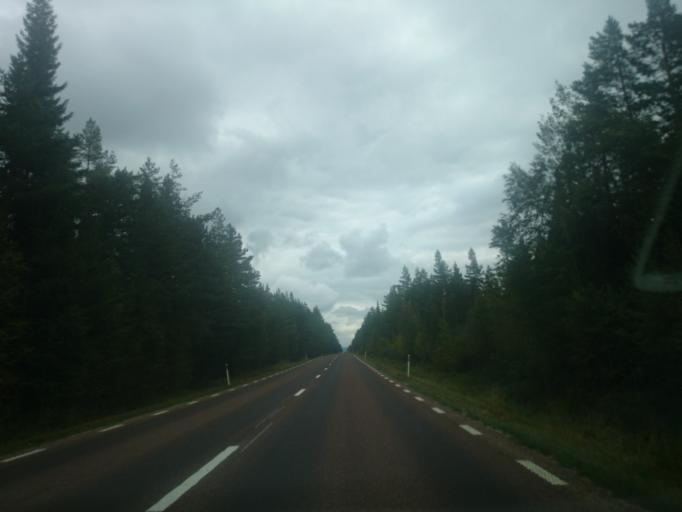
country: SE
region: Jaemtland
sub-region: Harjedalens Kommun
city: Sveg
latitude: 62.0480
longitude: 14.4900
